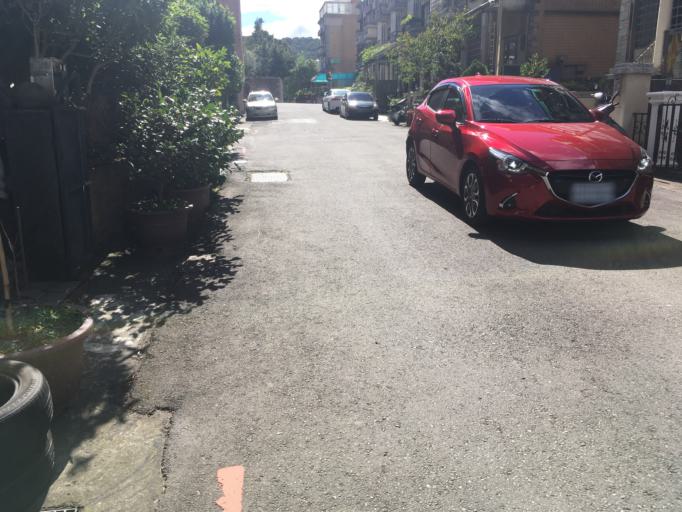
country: TW
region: Taiwan
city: Daxi
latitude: 24.9013
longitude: 121.1462
